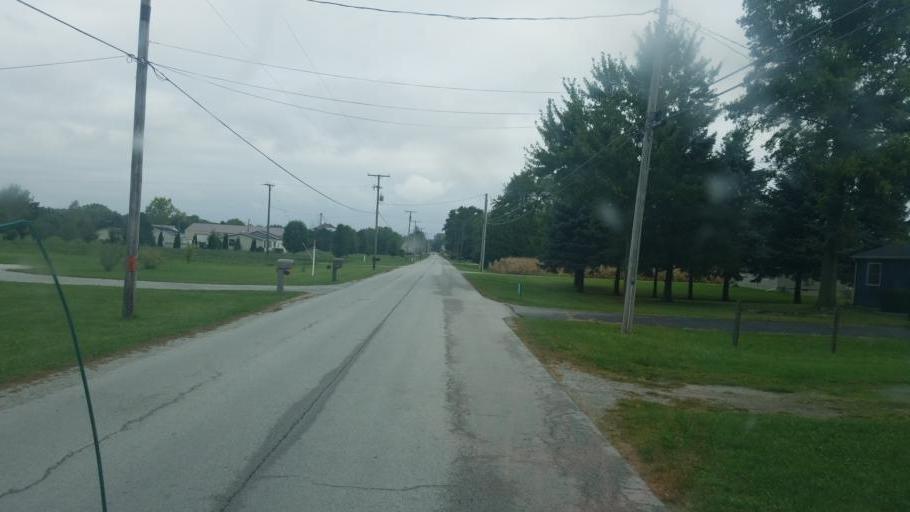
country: US
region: Ohio
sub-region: Wood County
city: Bowling Green
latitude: 41.2905
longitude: -83.6695
